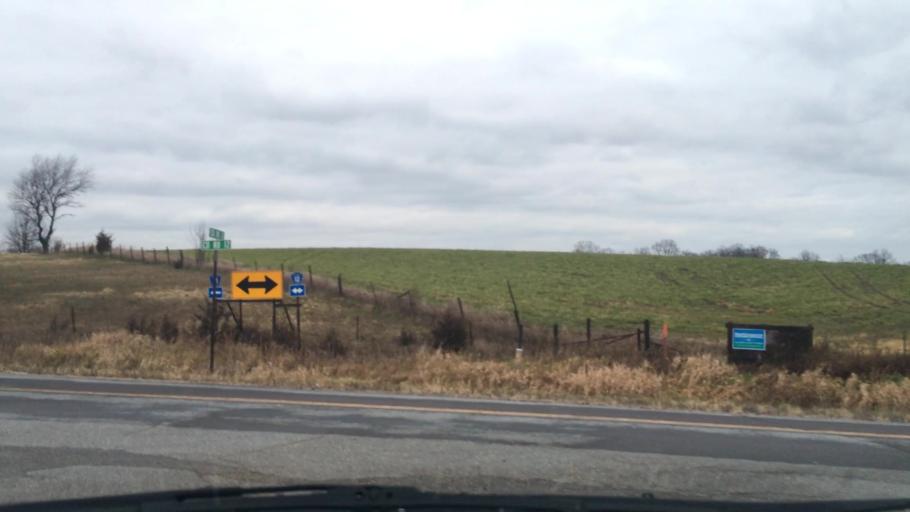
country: US
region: Minnesota
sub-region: Fillmore County
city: Harmony
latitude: 43.6469
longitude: -91.9254
